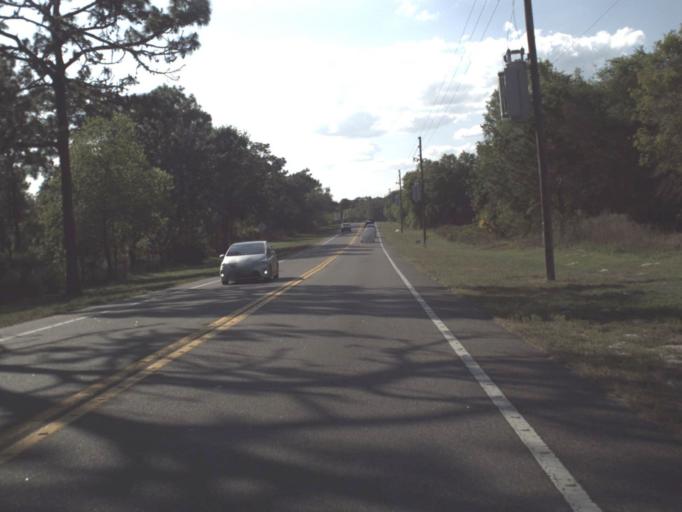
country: US
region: Florida
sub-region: Lake County
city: Mount Plymouth
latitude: 28.8145
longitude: -81.4695
